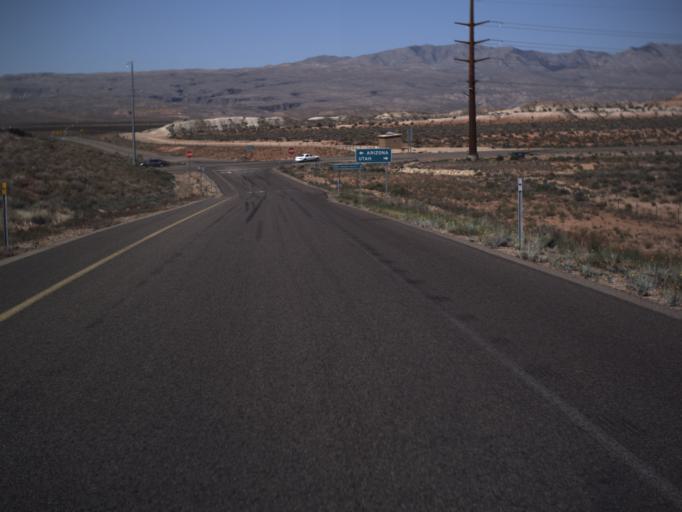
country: US
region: Utah
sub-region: Washington County
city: Saint George
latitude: 37.0010
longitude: -113.5576
